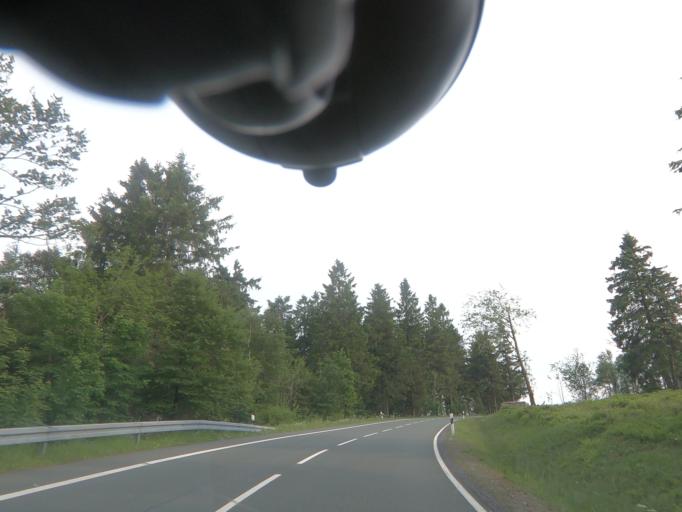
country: DE
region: North Rhine-Westphalia
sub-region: Regierungsbezirk Arnsberg
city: Winterberg
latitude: 51.1807
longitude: 8.4916
